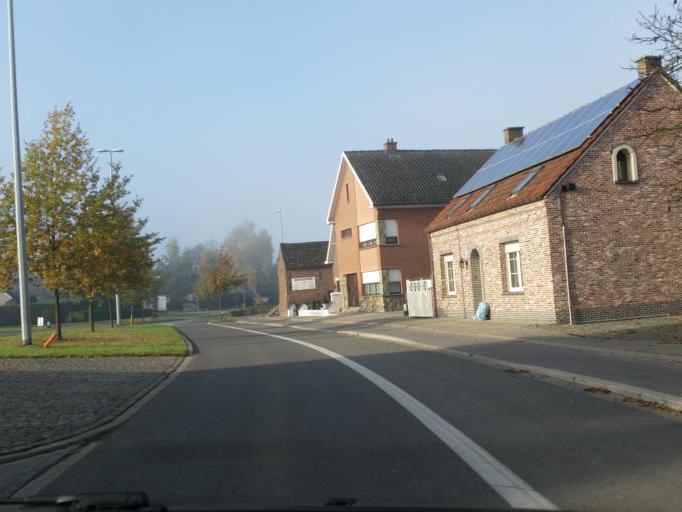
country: BE
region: Flanders
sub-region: Provincie Oost-Vlaanderen
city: Lebbeke
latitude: 50.9511
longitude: 4.1312
